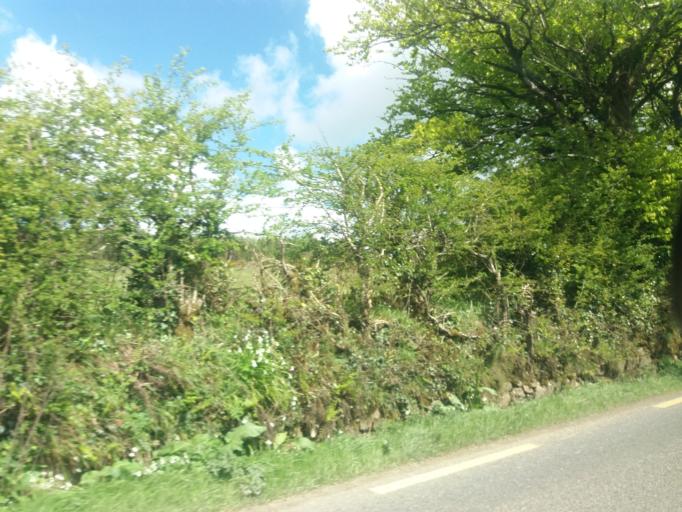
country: IE
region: Leinster
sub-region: Loch Garman
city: Loch Garman
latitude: 52.2946
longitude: -6.5755
